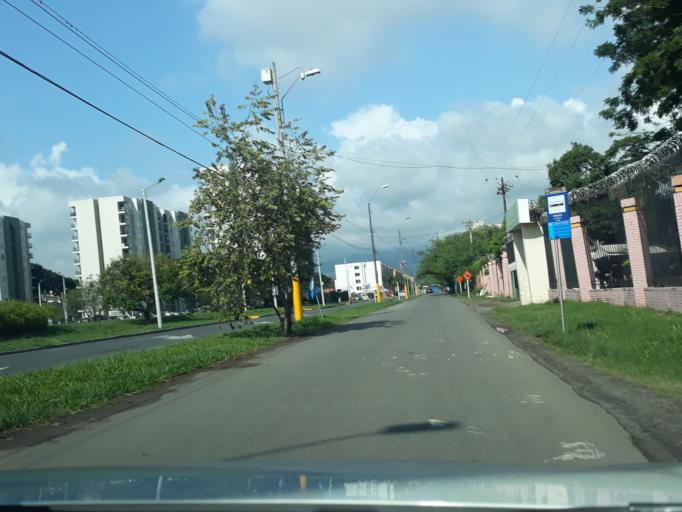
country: CO
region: Valle del Cauca
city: Cali
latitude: 3.3585
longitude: -76.5139
